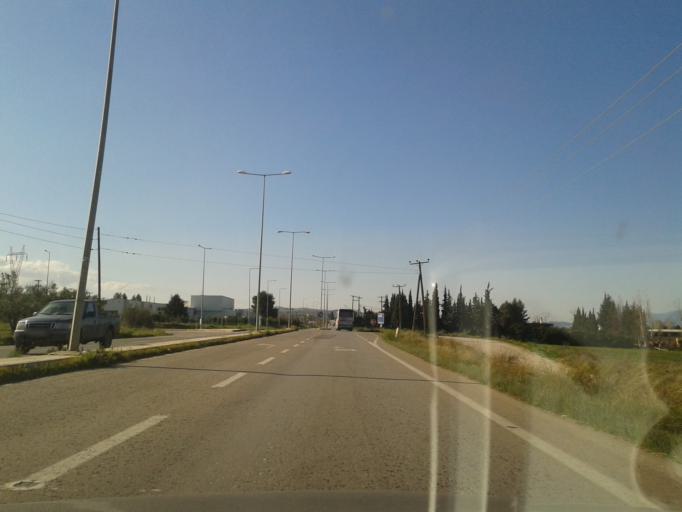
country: GR
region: Central Greece
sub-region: Nomos Voiotias
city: Thivai
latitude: 38.3378
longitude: 23.3486
